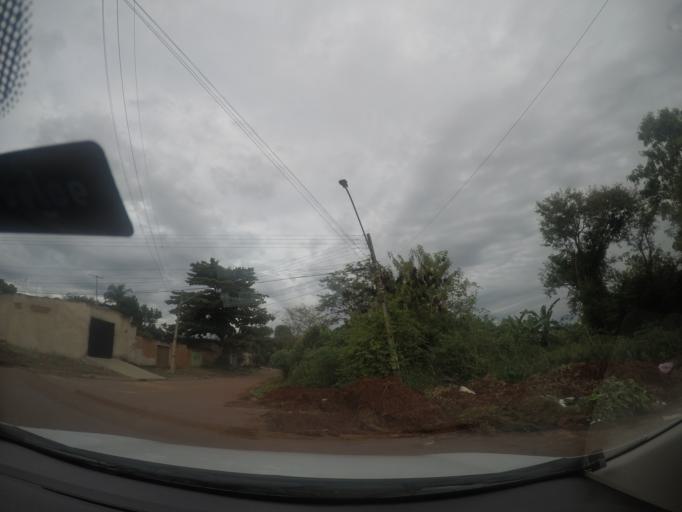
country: BR
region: Goias
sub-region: Goiania
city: Goiania
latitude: -16.5957
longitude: -49.3031
